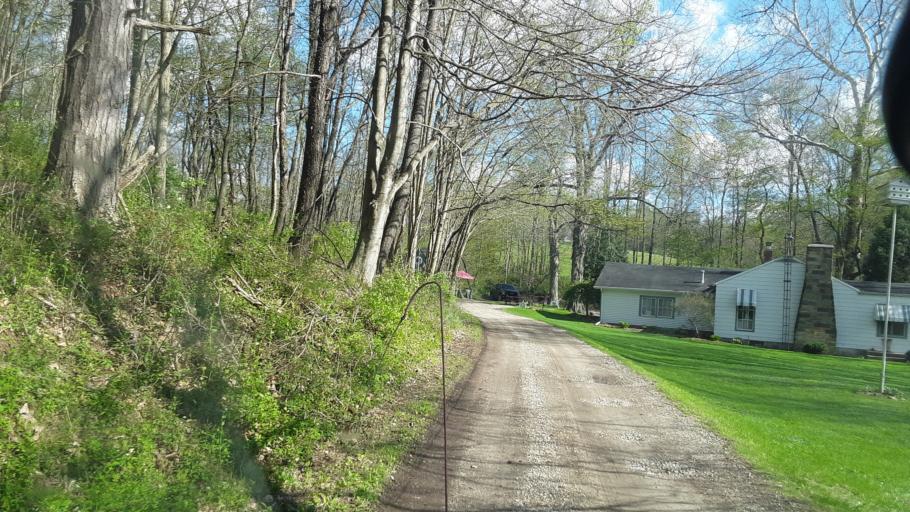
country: US
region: Ohio
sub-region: Knox County
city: Gambier
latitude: 40.4702
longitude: -82.4072
